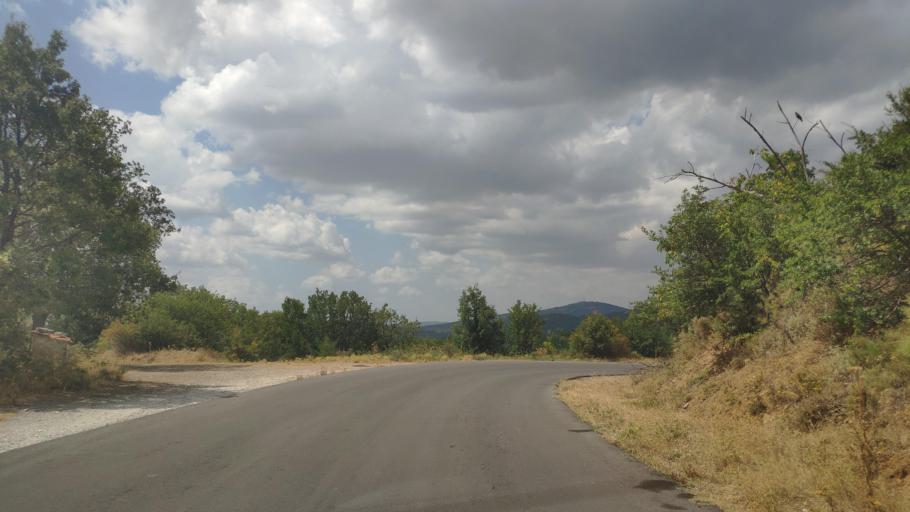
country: GR
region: Peloponnese
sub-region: Nomos Lakonias
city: Kariai
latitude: 37.2761
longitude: 22.5174
